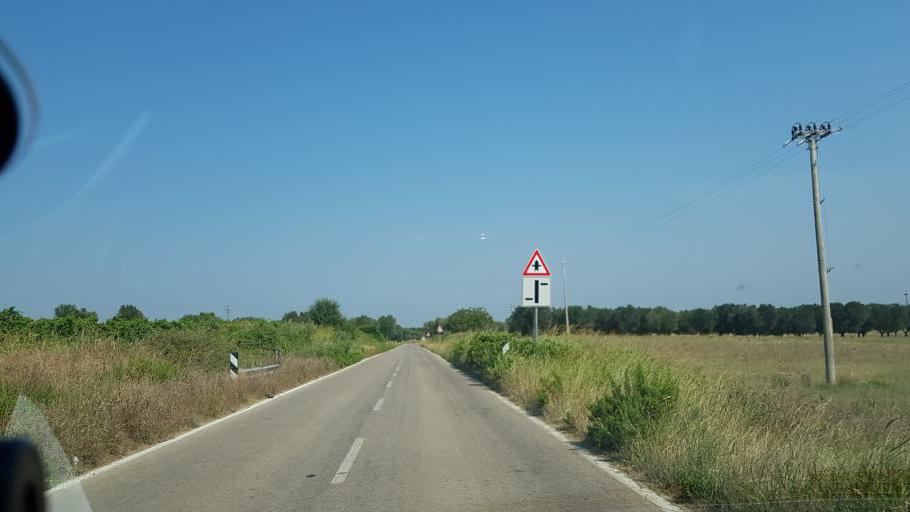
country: IT
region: Apulia
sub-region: Provincia di Brindisi
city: Torre Santa Susanna
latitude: 40.4989
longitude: 17.7286
